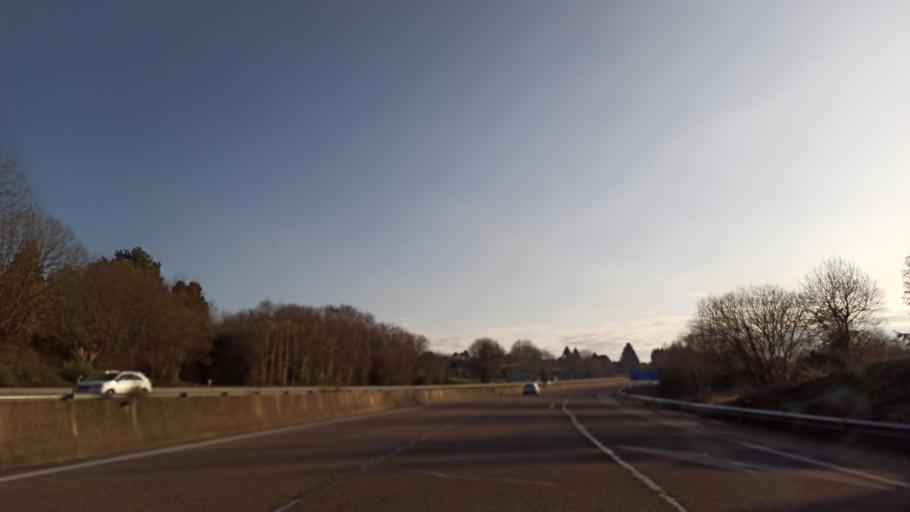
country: ES
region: Galicia
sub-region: Provincia da Coruna
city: Bergondo
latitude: 43.2954
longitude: -8.2753
